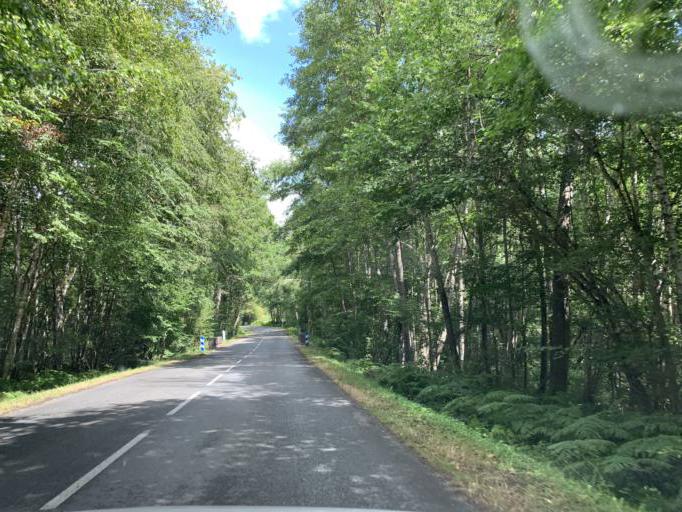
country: FR
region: Bourgogne
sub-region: Departement de la Nievre
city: Saint-Amand-en-Puisaye
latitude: 47.5837
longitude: 3.1606
